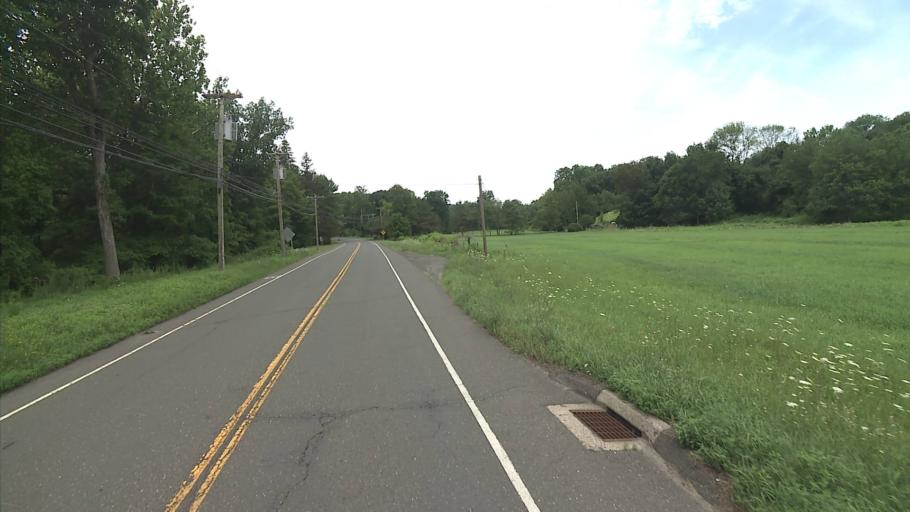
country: US
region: Connecticut
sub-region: Litchfield County
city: New Milford
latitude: 41.5492
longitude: -73.3377
